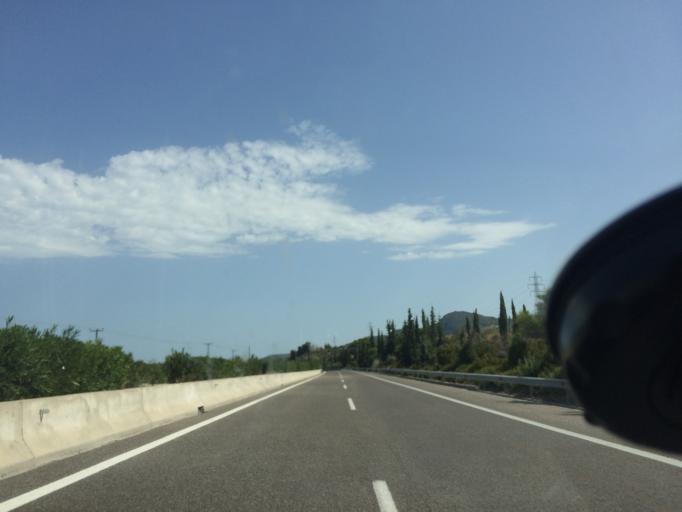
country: GR
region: Central Greece
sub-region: Nomos Fthiotidos
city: Livanates
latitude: 38.7457
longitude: 22.9621
